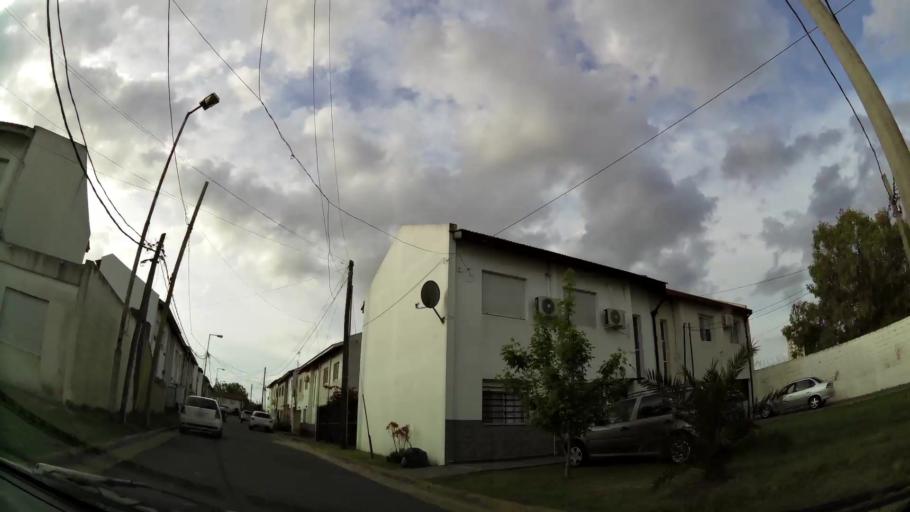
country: AR
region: Buenos Aires
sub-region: Partido de Quilmes
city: Quilmes
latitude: -34.7444
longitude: -58.2524
